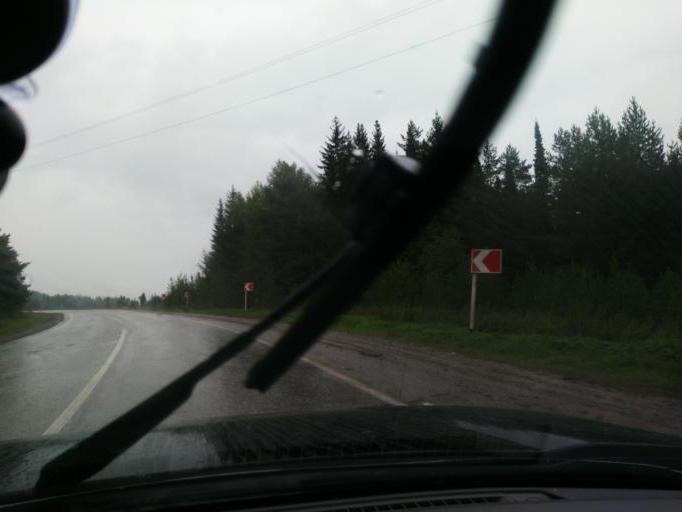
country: RU
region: Perm
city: Osa
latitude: 57.3057
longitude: 55.6196
